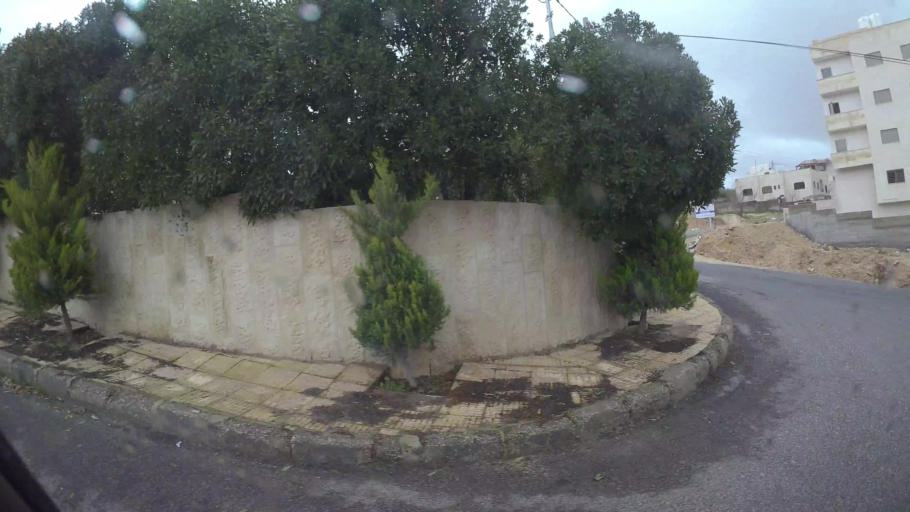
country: JO
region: Amman
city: Al Jubayhah
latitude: 32.0611
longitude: 35.8870
